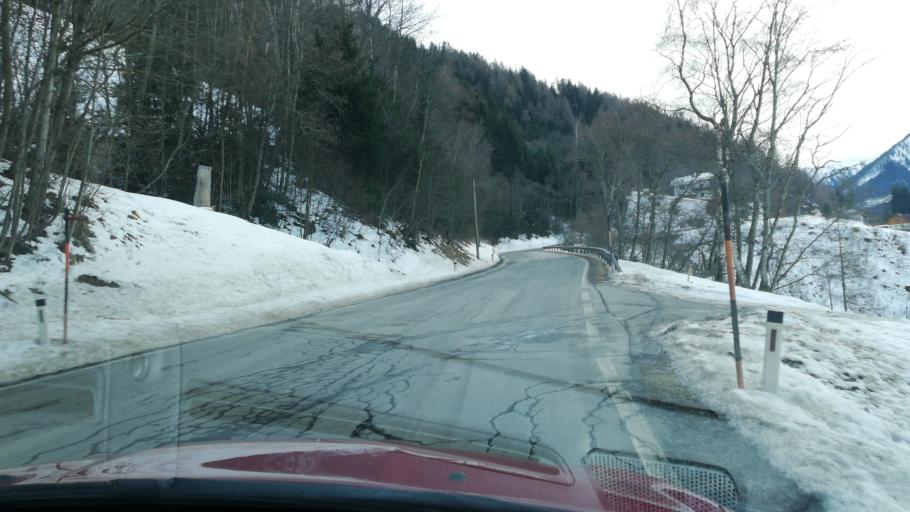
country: AT
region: Styria
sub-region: Politischer Bezirk Liezen
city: Donnersbach
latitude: 47.4470
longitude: 14.1433
